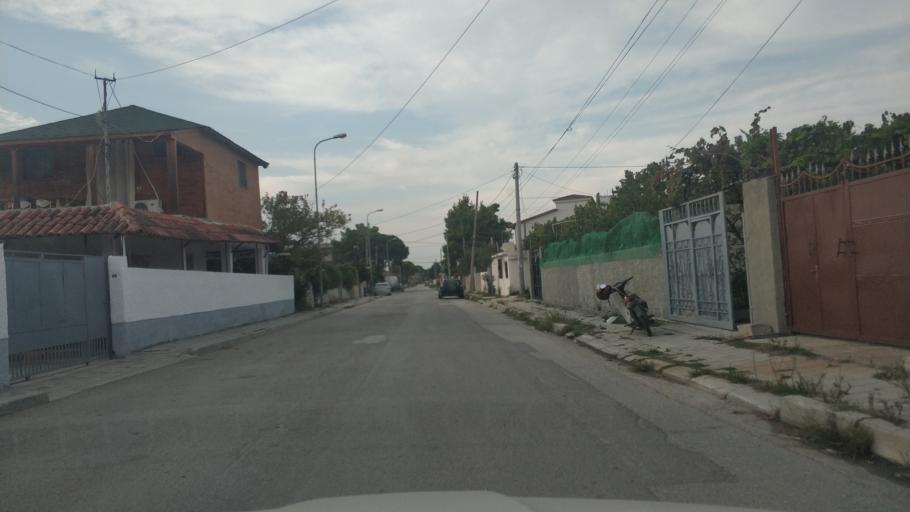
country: AL
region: Vlore
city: Vlore
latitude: 40.4623
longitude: 19.4677
